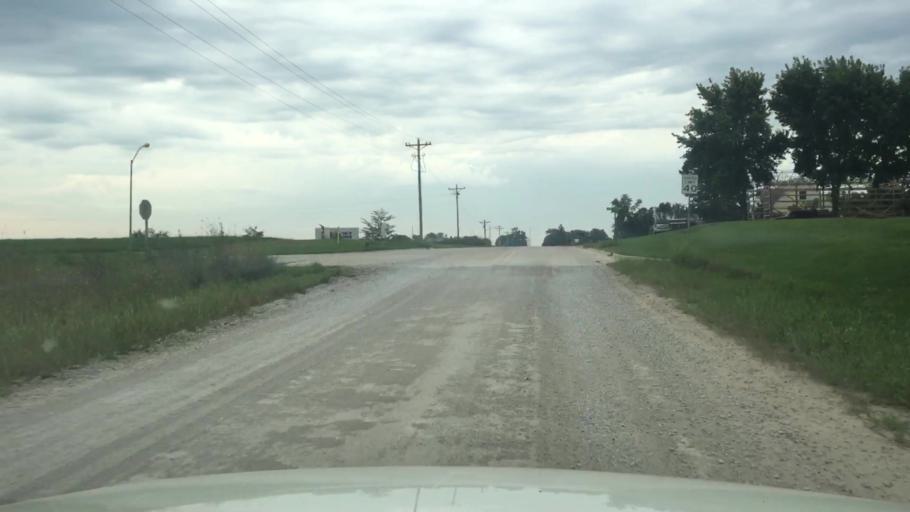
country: US
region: Iowa
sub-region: Story County
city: Huxley
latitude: 41.8862
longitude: -93.5810
